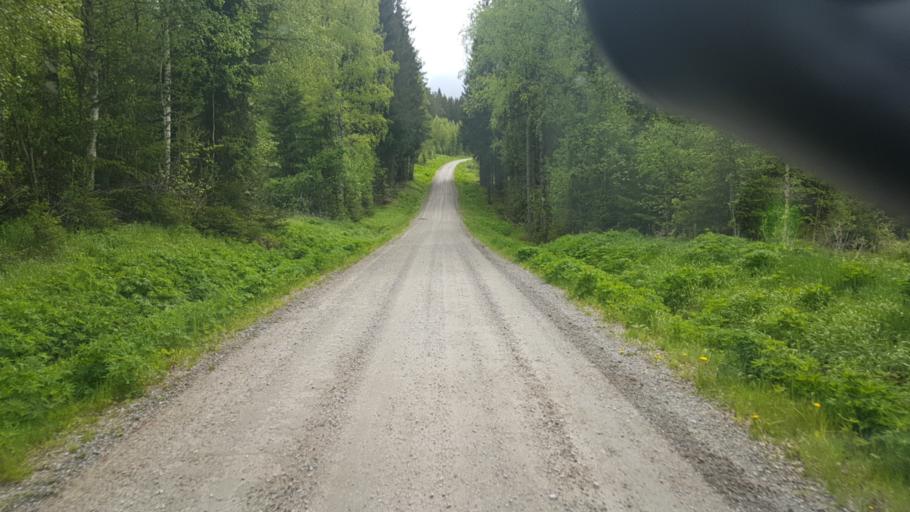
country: SE
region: Vaermland
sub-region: Arvika Kommun
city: Arvika
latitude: 59.8383
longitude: 12.7610
